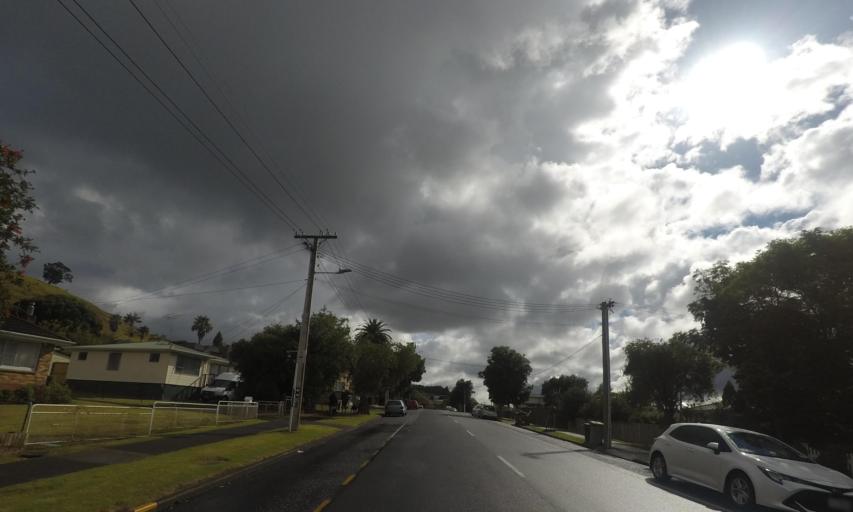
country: NZ
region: Auckland
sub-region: Auckland
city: Mangere
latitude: -36.9528
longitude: 174.7861
